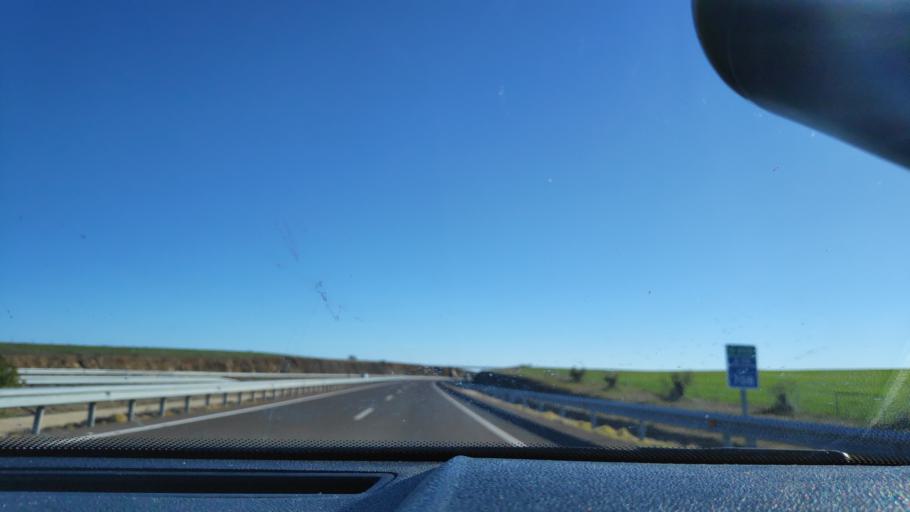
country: ES
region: Extremadura
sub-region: Provincia de Badajoz
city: Fuente de Cantos
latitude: 38.1945
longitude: -6.2822
